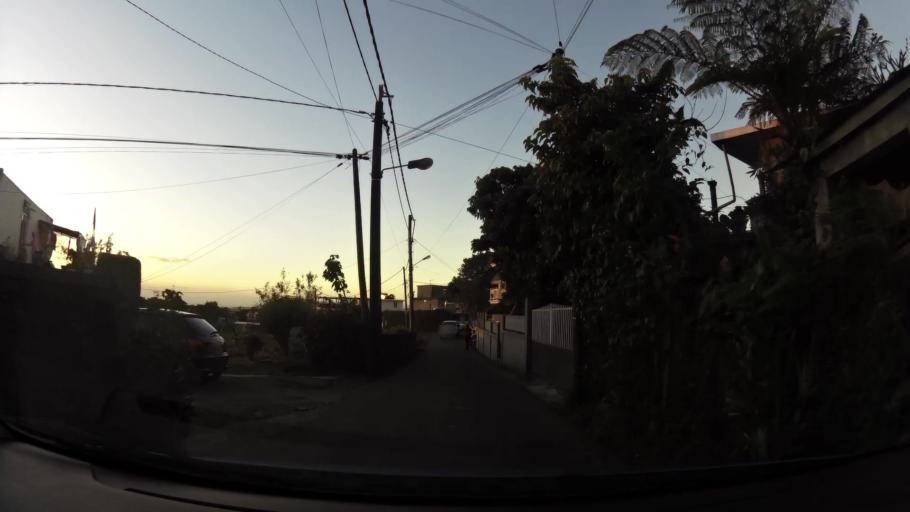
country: MU
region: Plaines Wilhems
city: Curepipe
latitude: -20.2992
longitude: 57.5234
